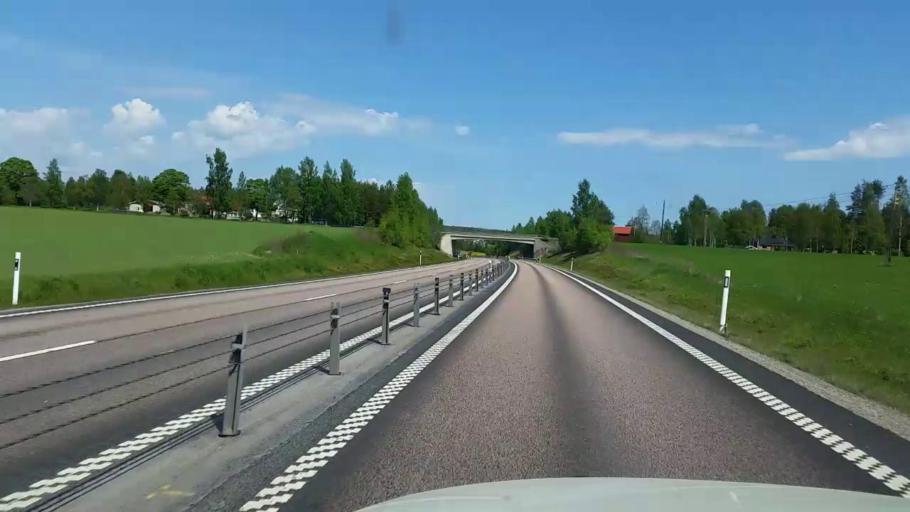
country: SE
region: Gaevleborg
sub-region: Hudiksvalls Kommun
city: Hudiksvall
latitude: 61.7586
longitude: 17.0908
